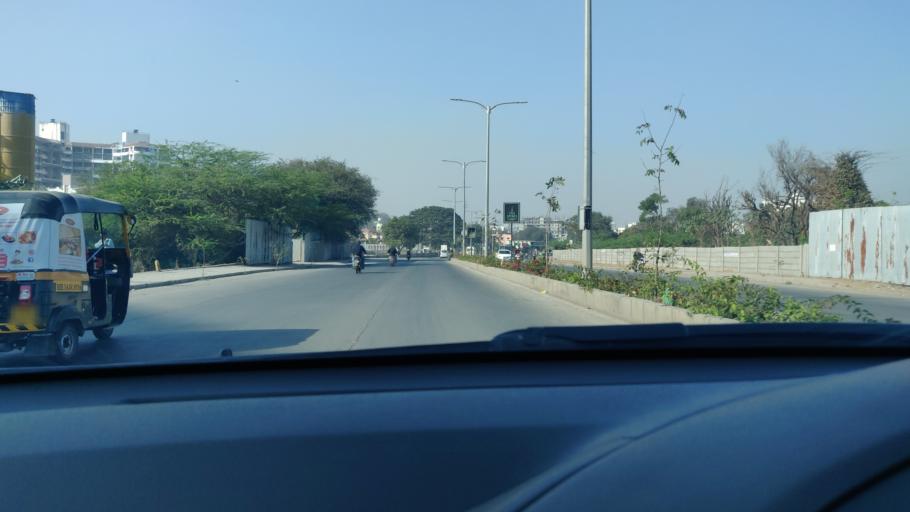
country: IN
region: Maharashtra
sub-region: Pune Division
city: Khadki
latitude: 18.5623
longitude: 73.7941
